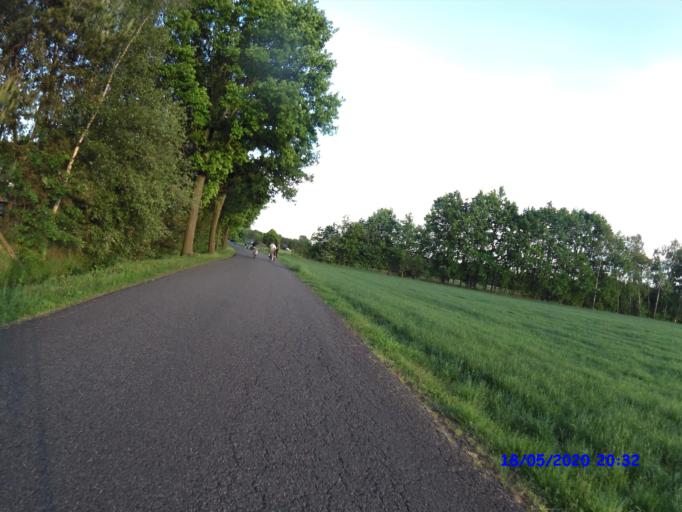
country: BE
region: Flanders
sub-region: Provincie Antwerpen
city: Kasterlee
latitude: 51.1979
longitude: 4.9518
